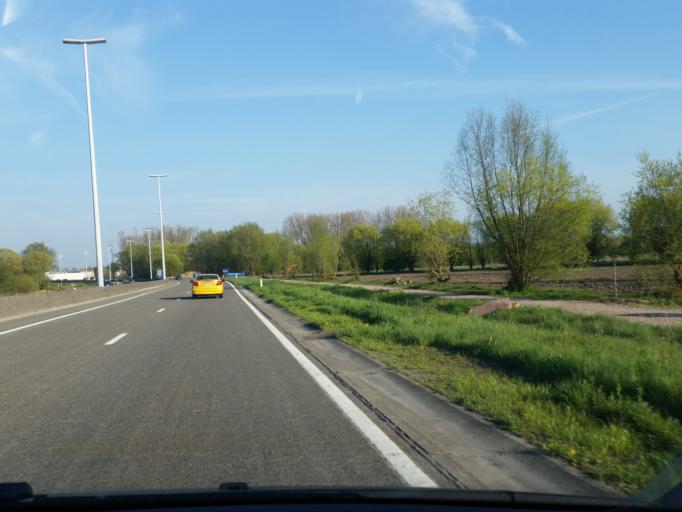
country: BE
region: Flanders
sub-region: Provincie Antwerpen
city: Willebroek
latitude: 51.0453
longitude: 4.3468
